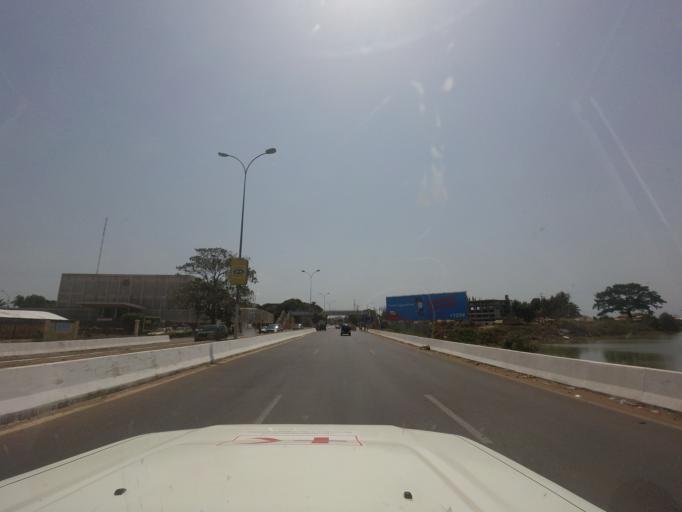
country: GN
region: Conakry
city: Camayenne
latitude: 9.5214
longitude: -13.6922
